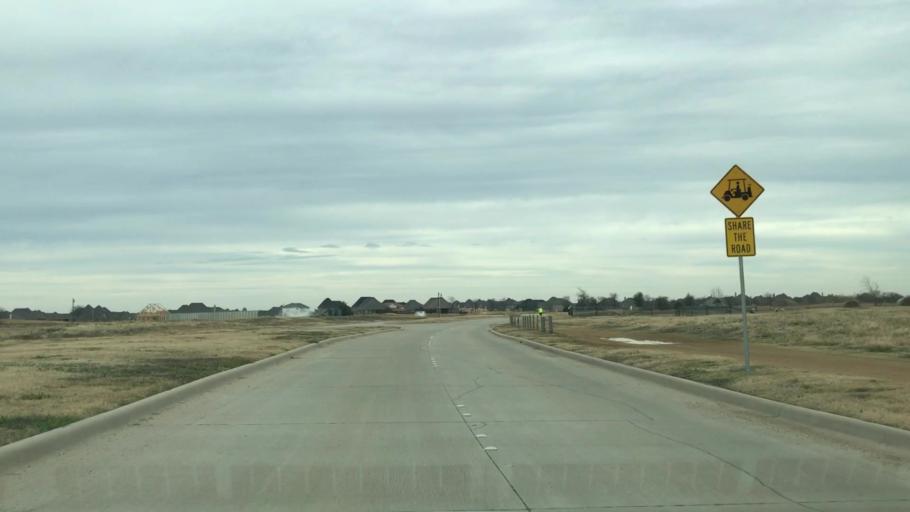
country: US
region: Texas
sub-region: Denton County
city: The Colony
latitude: 33.1029
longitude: -96.9265
